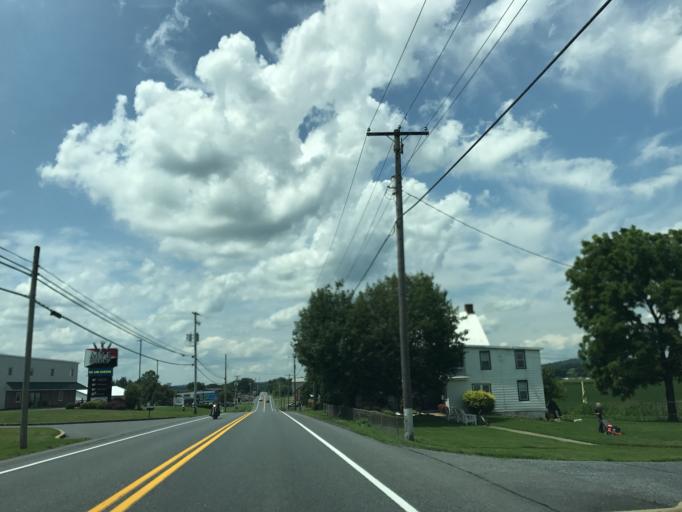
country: US
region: Pennsylvania
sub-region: Lancaster County
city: Clay
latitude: 40.2112
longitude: -76.2326
